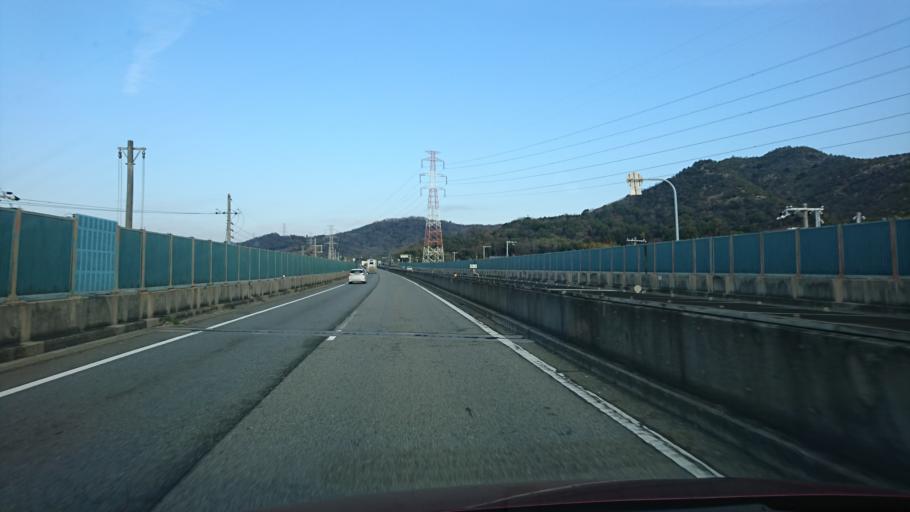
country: JP
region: Hyogo
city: Himeji
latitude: 34.8411
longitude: 134.7374
